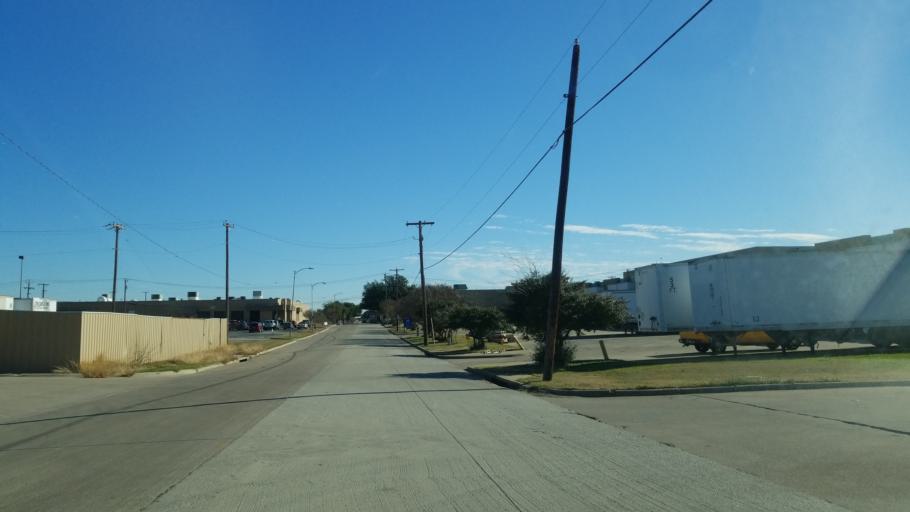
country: US
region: Texas
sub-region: Dallas County
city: Grand Prairie
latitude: 32.7447
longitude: -97.0517
